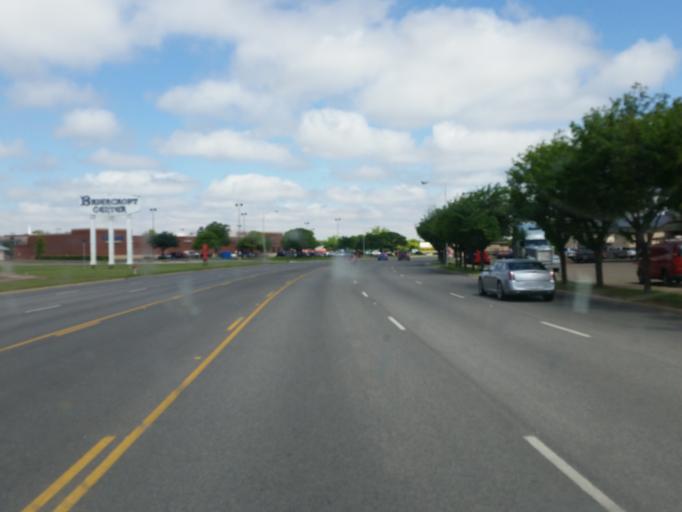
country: US
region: Texas
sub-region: Lubbock County
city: Lubbock
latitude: 33.5462
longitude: -101.8537
